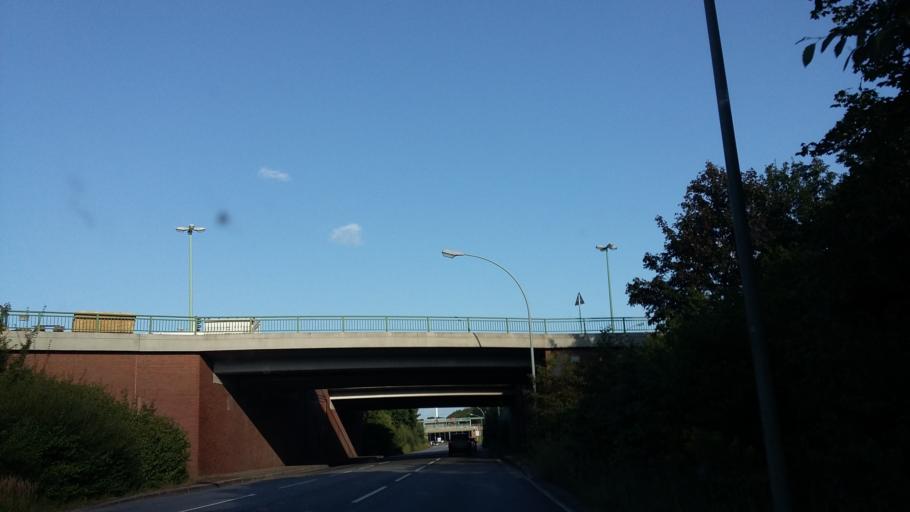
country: DE
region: Bremen
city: Bremerhaven
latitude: 53.5508
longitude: 8.5926
